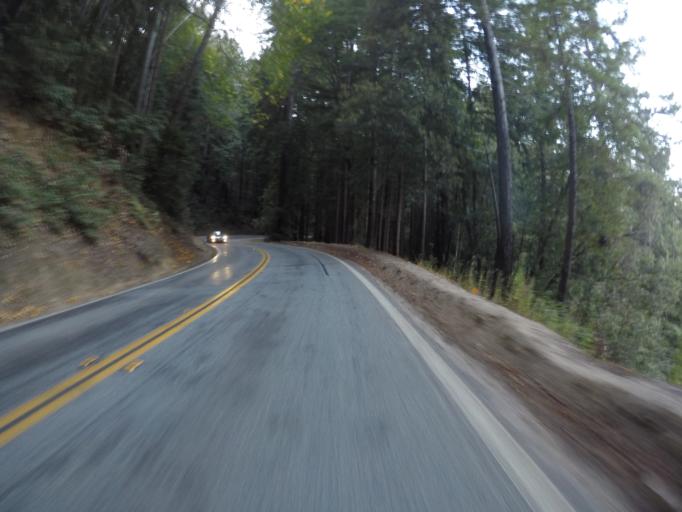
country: US
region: California
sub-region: Santa Cruz County
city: Pasatiempo
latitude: 37.0145
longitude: -122.0609
